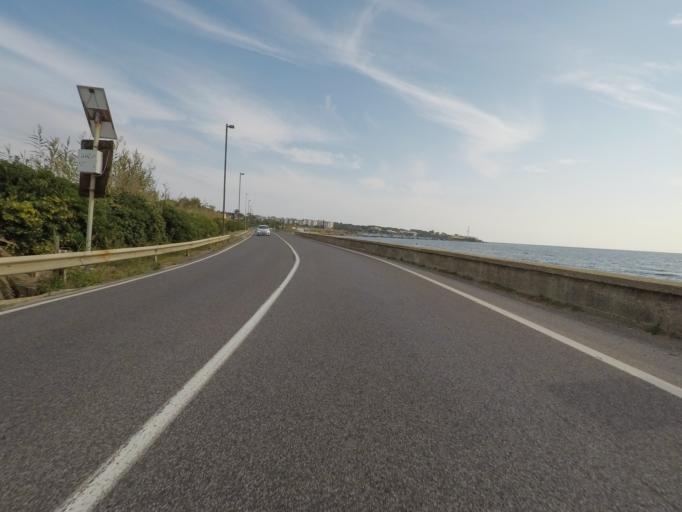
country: IT
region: Latium
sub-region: Citta metropolitana di Roma Capitale
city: Santa Marinella
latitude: 42.0400
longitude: 11.8293
